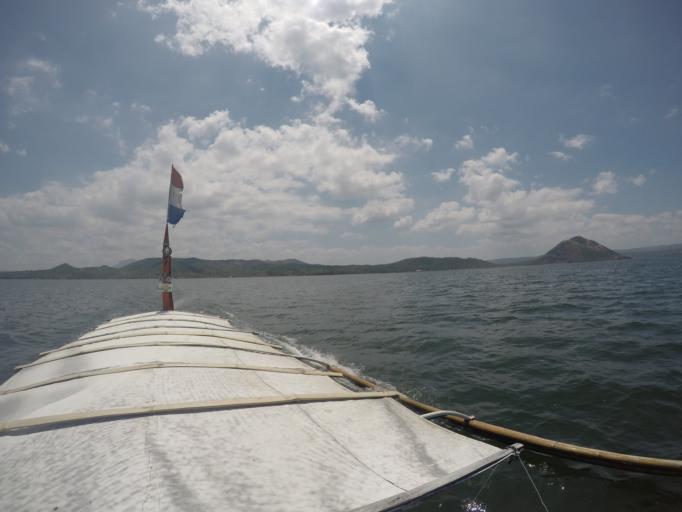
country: PH
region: Calabarzon
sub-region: Province of Batangas
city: Sampaloc
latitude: 14.0504
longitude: 120.9980
